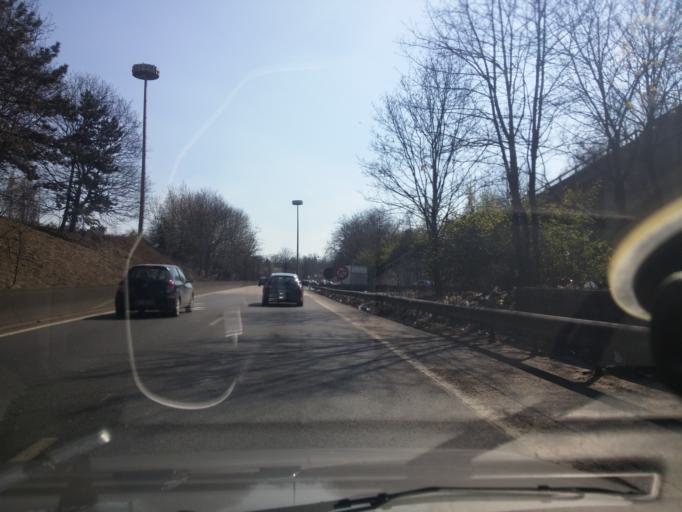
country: FR
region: Ile-de-France
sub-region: Departement du Val-de-Marne
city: Cachan
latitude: 48.7962
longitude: 2.3440
